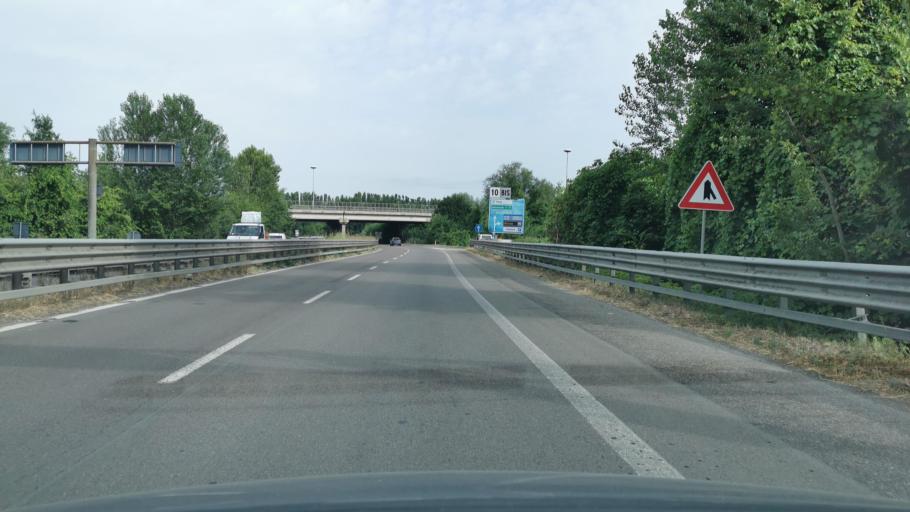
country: IT
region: Emilia-Romagna
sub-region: Provincia di Modena
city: Villanova
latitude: 44.6703
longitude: 10.9277
